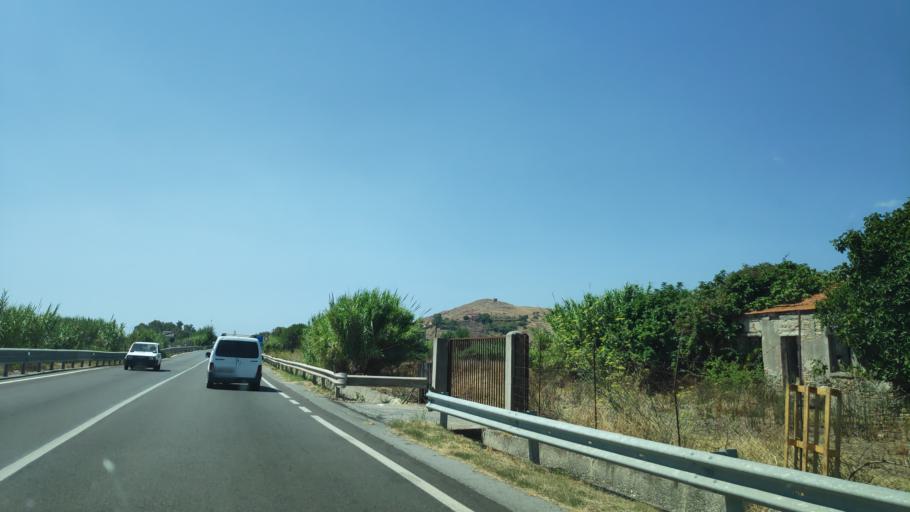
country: IT
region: Calabria
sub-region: Provincia di Reggio Calabria
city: Brancaleone-Marina
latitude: 37.9850
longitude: 16.1168
